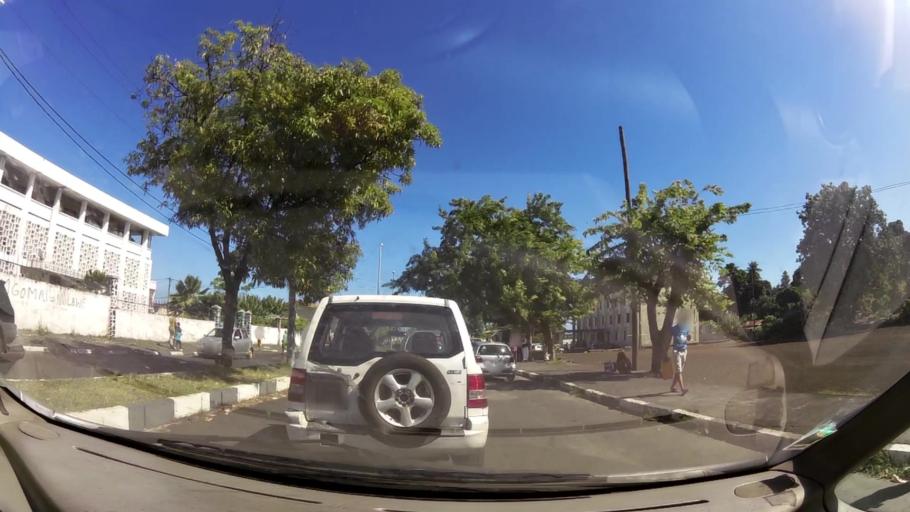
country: KM
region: Grande Comore
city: Moroni
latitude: -11.7020
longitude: 43.2538
